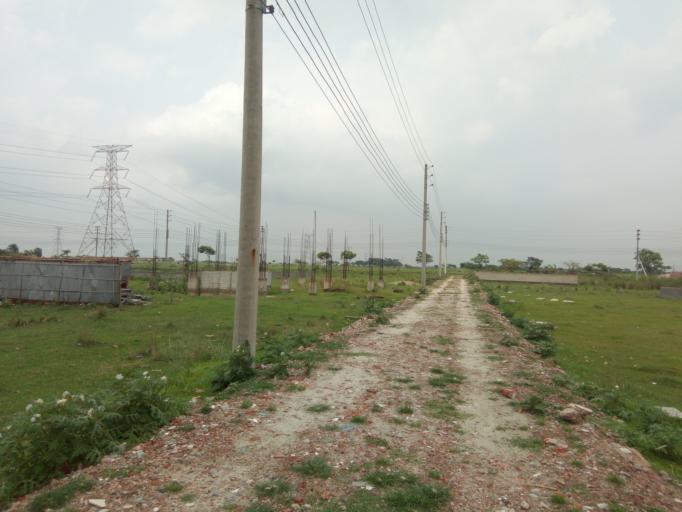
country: BD
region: Dhaka
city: Paltan
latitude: 23.7669
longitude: 90.4480
